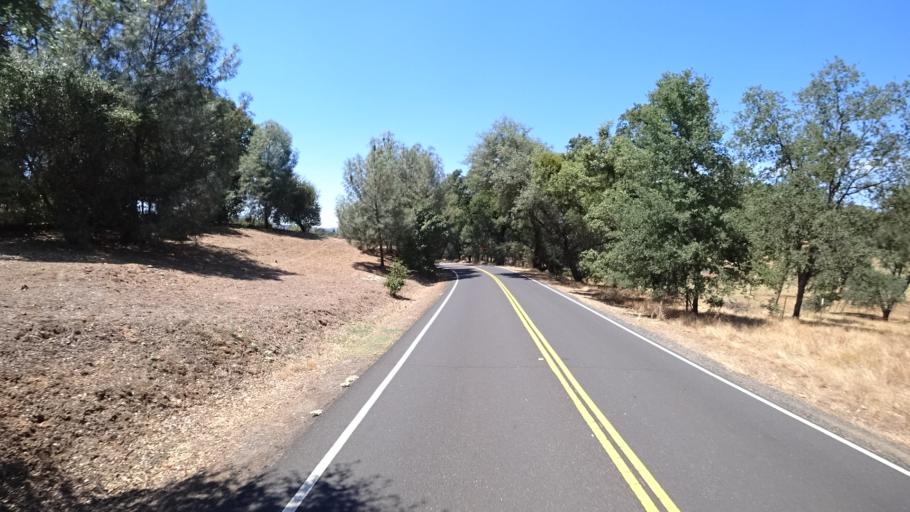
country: US
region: California
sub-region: Calaveras County
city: Angels Camp
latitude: 38.0771
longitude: -120.5620
